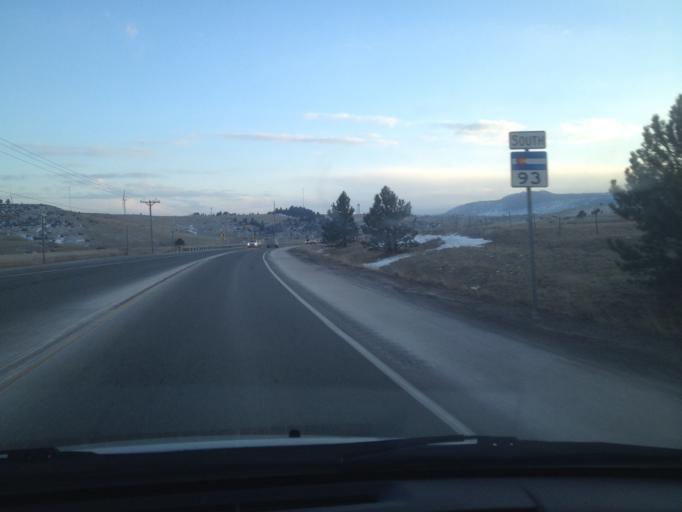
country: US
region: Colorado
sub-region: Boulder County
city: Superior
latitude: 39.9275
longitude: -105.2345
